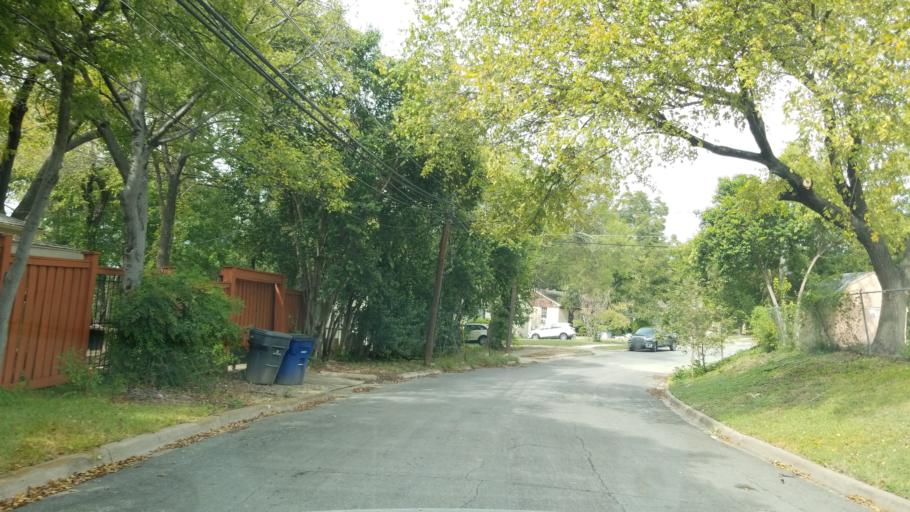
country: US
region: Texas
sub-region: Dallas County
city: Dallas
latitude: 32.7718
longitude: -96.7225
